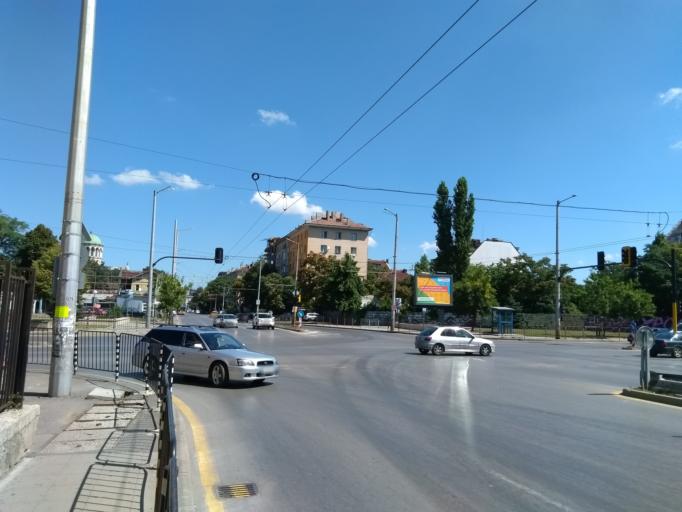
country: BG
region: Sofia-Capital
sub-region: Stolichna Obshtina
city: Sofia
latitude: 42.6997
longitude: 23.3099
